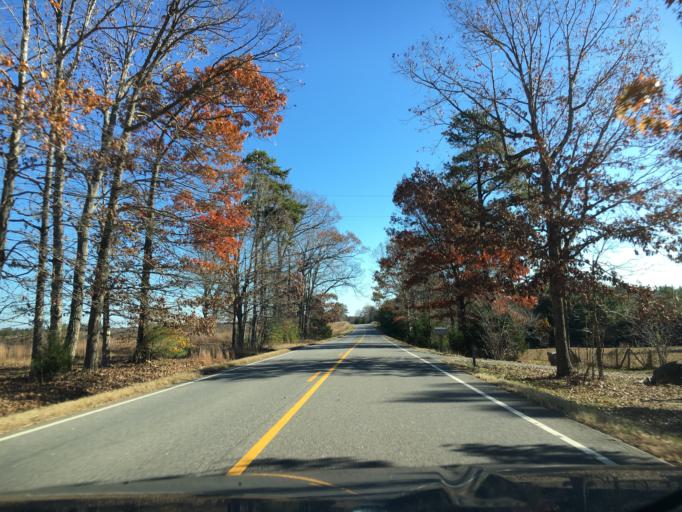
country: US
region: Virginia
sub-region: Appomattox County
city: Appomattox
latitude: 37.4564
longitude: -78.6927
